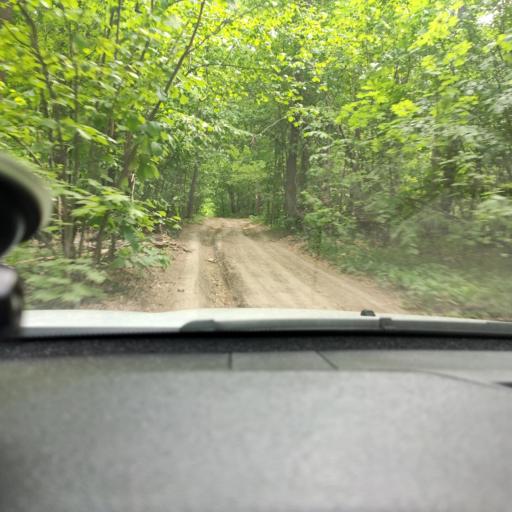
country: RU
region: Samara
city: Samara
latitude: 53.3209
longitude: 50.2127
